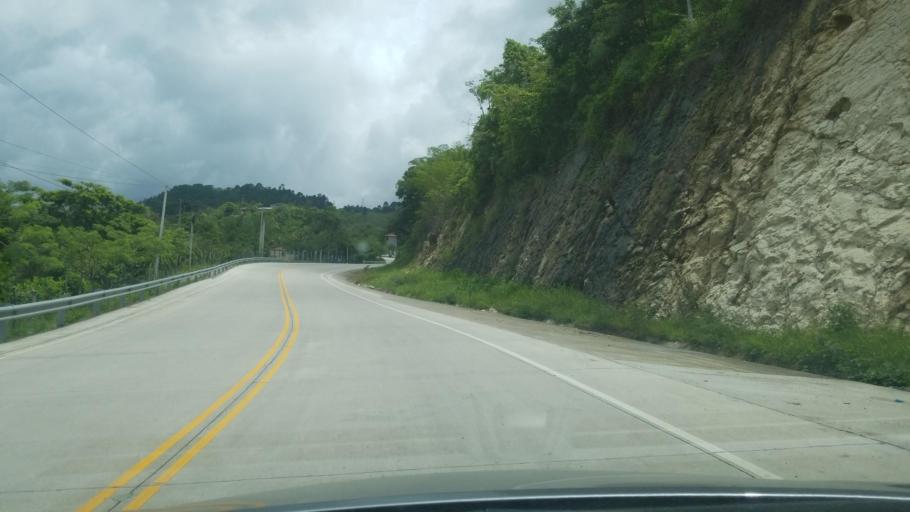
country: HN
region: Copan
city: San Jeronimo
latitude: 14.9879
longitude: -88.8479
